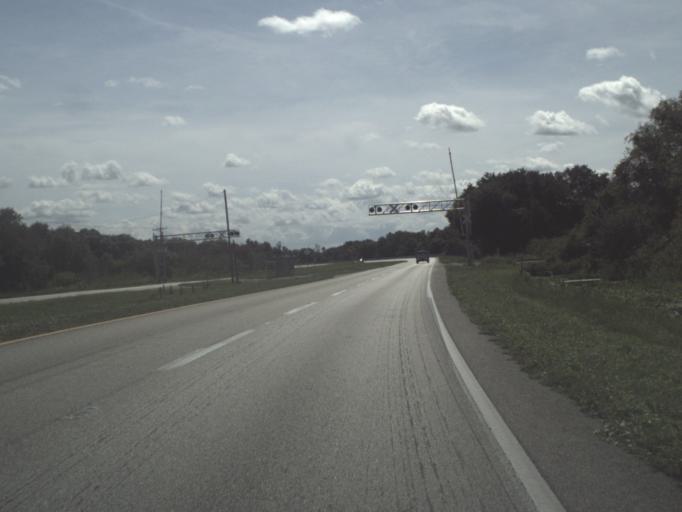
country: US
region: Florida
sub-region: Glades County
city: Moore Haven
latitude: 26.8973
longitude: -81.2384
